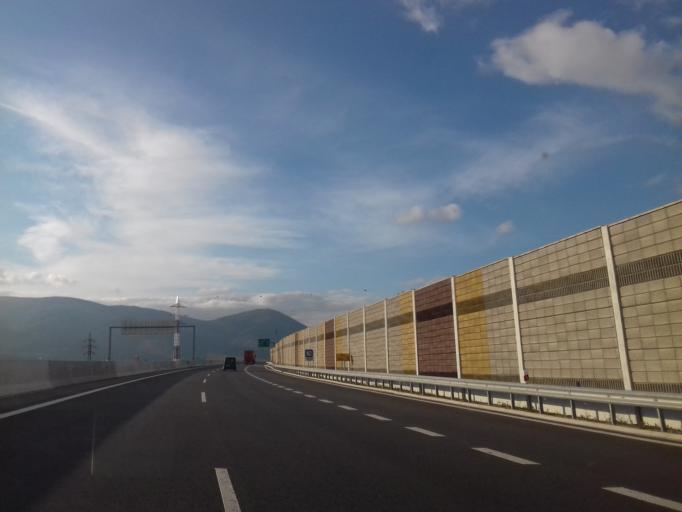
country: SK
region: Zilinsky
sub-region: Okres Zilina
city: Vrutky
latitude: 49.1099
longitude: 18.9518
